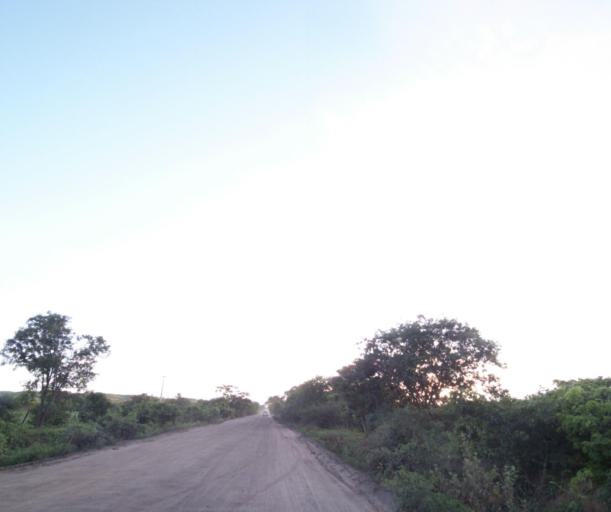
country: BR
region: Bahia
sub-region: Sao Felix Do Coribe
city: Santa Maria da Vitoria
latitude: -13.6204
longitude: -44.4142
